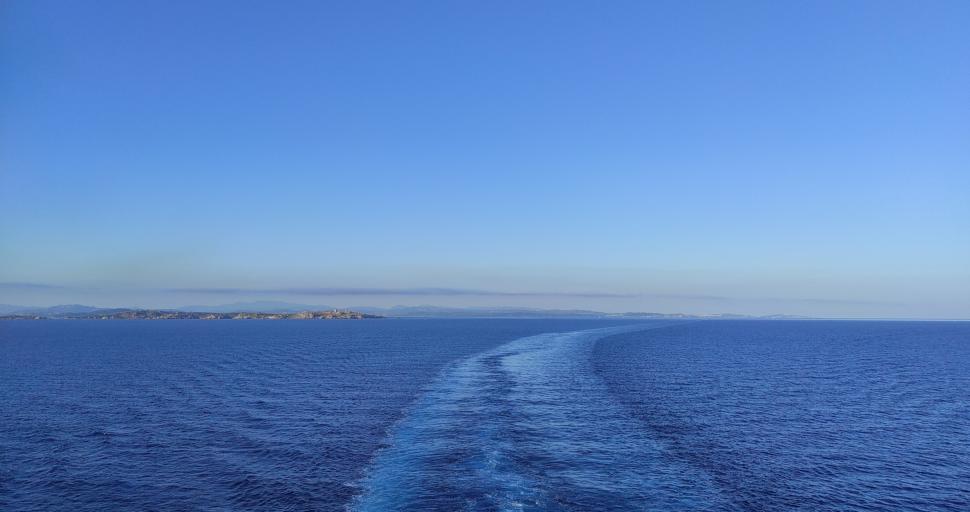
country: IT
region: Sardinia
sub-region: Provincia di Olbia-Tempio
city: La Maddalena
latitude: 41.3520
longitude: 9.3626
